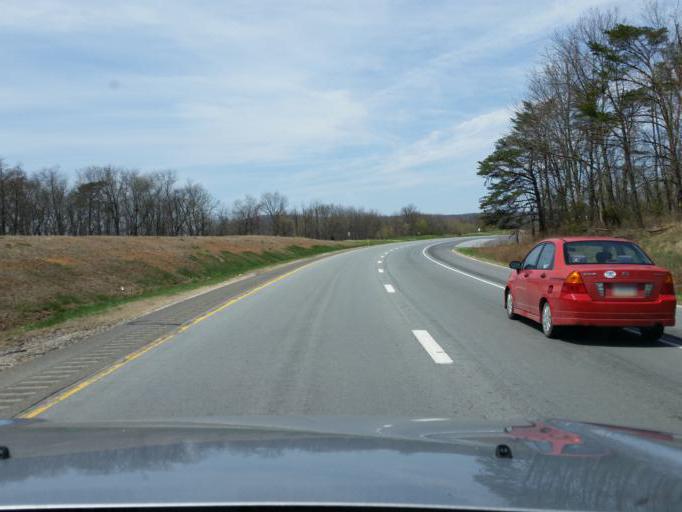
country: US
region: Pennsylvania
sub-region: Perry County
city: Newport
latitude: 40.4796
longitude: -77.0699
